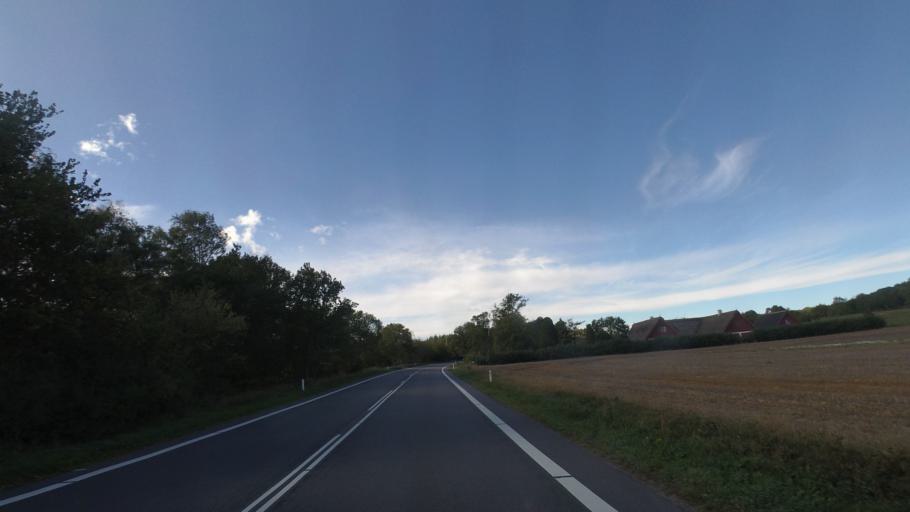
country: DK
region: Capital Region
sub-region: Bornholm Kommune
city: Ronne
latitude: 55.0797
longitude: 14.7589
